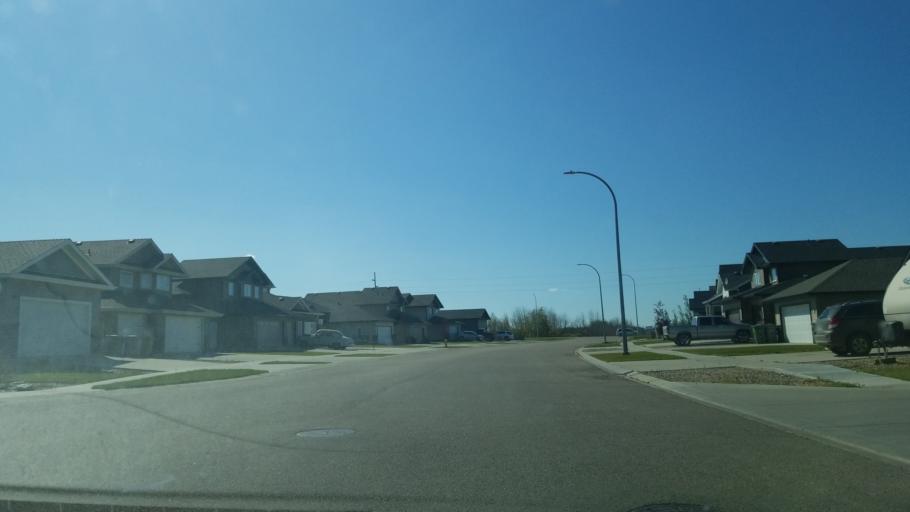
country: CA
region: Saskatchewan
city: Lloydminster
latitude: 53.2641
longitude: -110.0517
